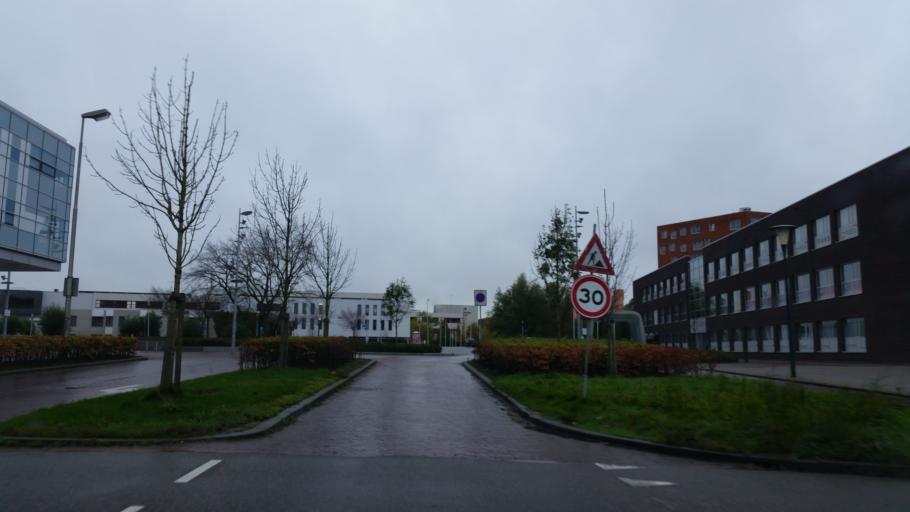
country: NL
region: Friesland
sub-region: Gemeente Leeuwarden
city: Bilgaard
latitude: 53.2125
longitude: 5.7976
